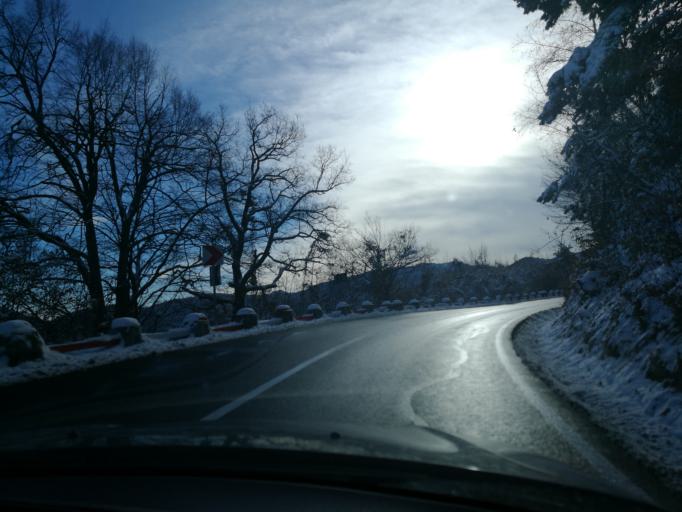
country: RO
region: Brasov
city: Brasov
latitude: 45.6379
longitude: 25.5642
